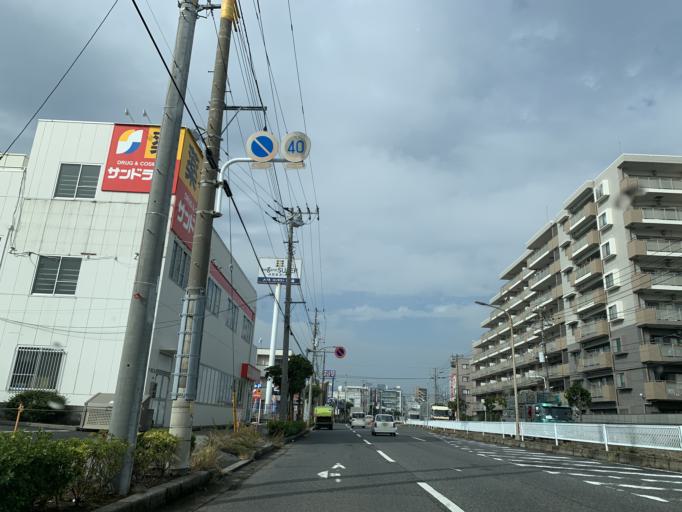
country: JP
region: Tokyo
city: Urayasu
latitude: 35.6691
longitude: 139.9036
